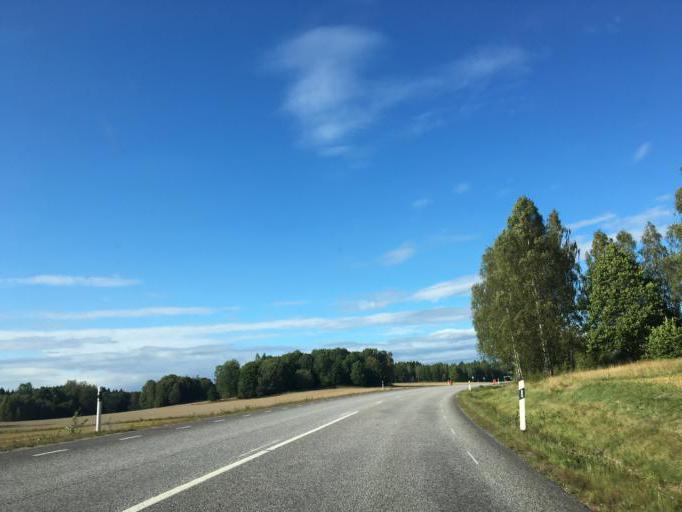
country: SE
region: Soedermanland
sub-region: Nykopings Kommun
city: Nykoping
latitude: 58.8025
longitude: 16.9482
